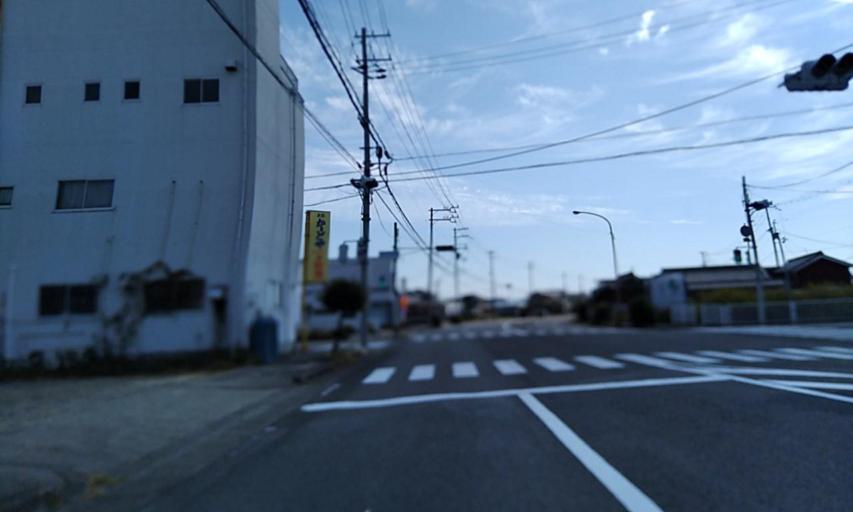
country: JP
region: Wakayama
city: Gobo
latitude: 33.9002
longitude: 135.1623
